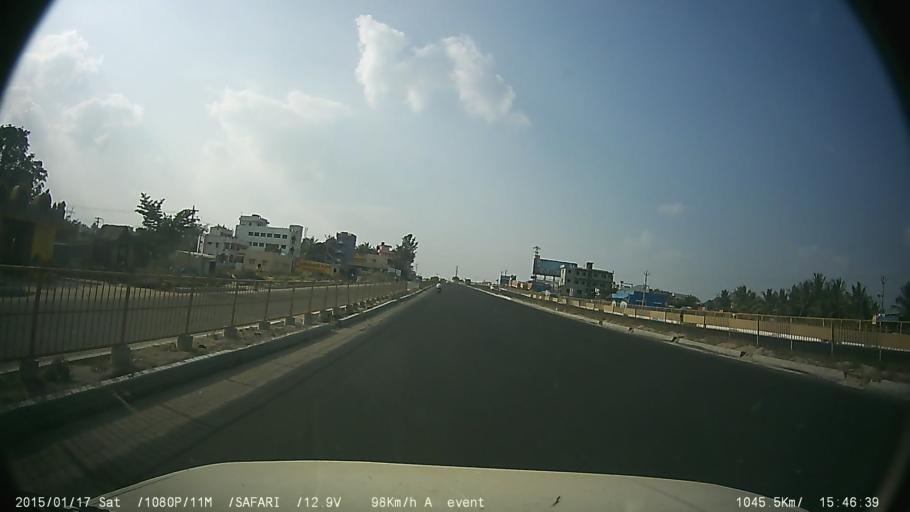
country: IN
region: Tamil Nadu
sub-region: Krishnagiri
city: Hosur
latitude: 12.7136
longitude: 77.8859
